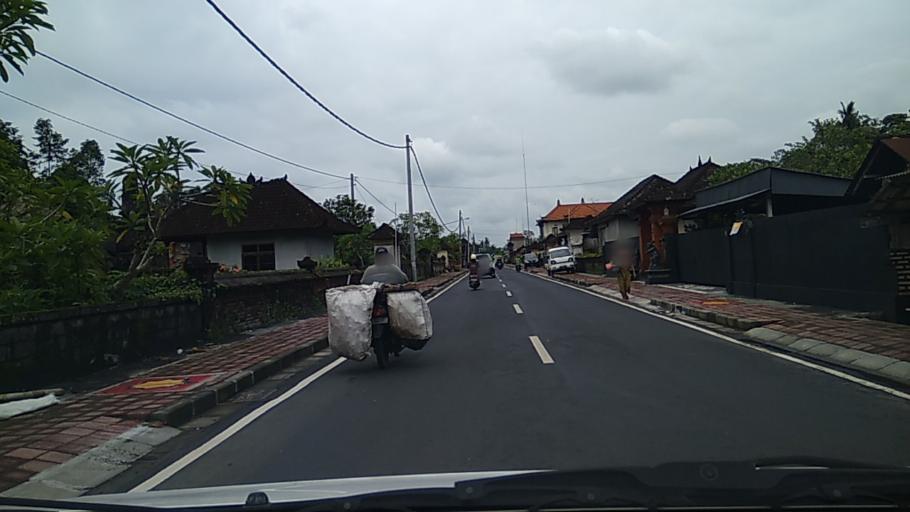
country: ID
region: Bali
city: Banjar Tebongkang
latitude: -8.5309
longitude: 115.2301
